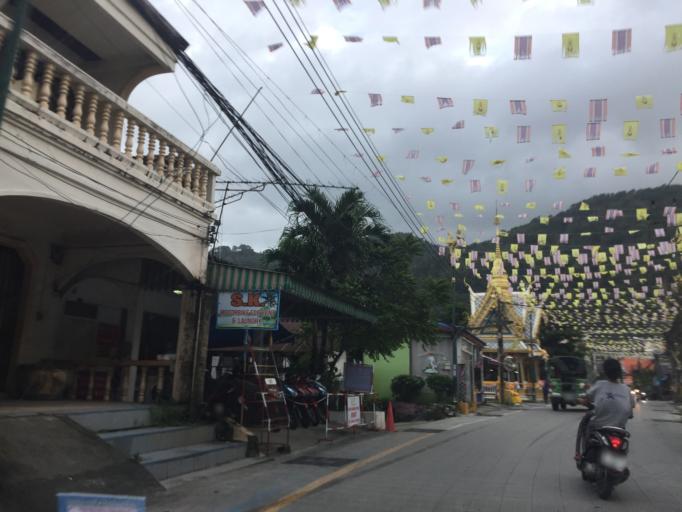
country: TH
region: Phuket
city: Patong
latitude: 7.8992
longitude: 98.3103
